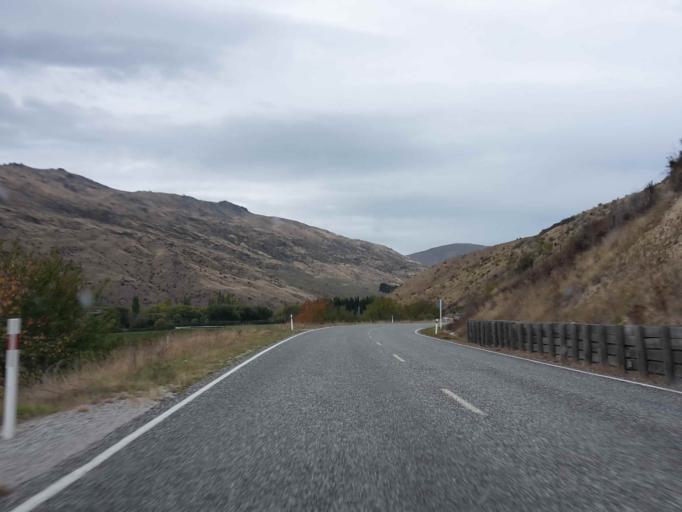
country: NZ
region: Otago
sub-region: Queenstown-Lakes District
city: Wanaka
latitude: -44.8221
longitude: 169.0623
